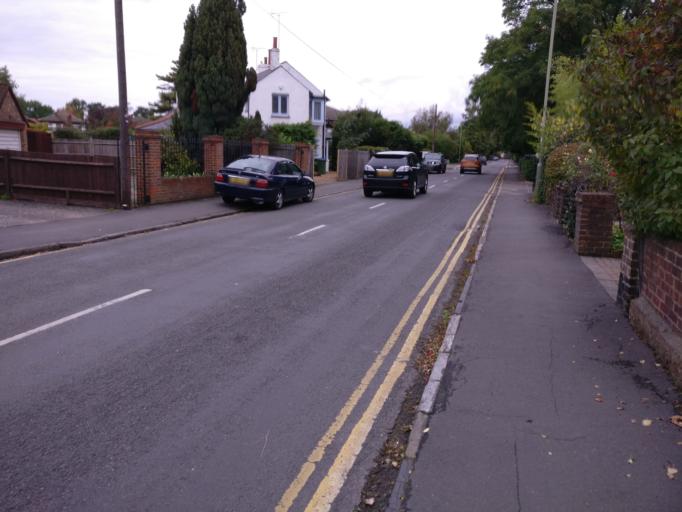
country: GB
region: England
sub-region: Surrey
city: Walton-on-Thames
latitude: 51.3772
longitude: -0.4077
